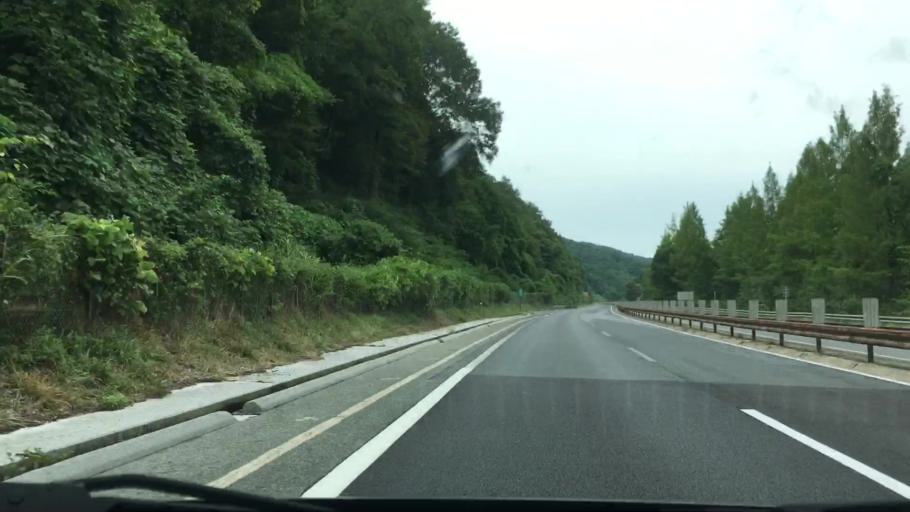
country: JP
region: Okayama
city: Niimi
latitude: 34.9741
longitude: 133.6215
